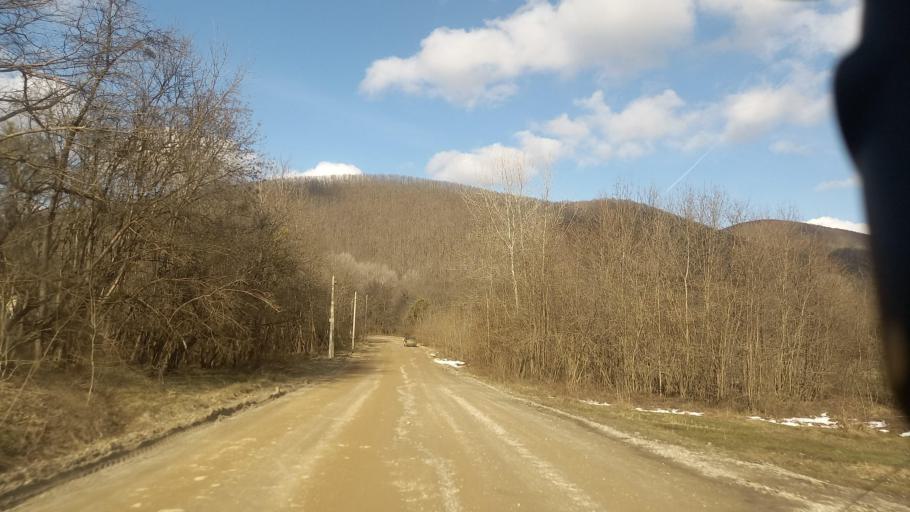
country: RU
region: Krasnodarskiy
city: Smolenskaya
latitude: 44.6017
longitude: 38.8435
